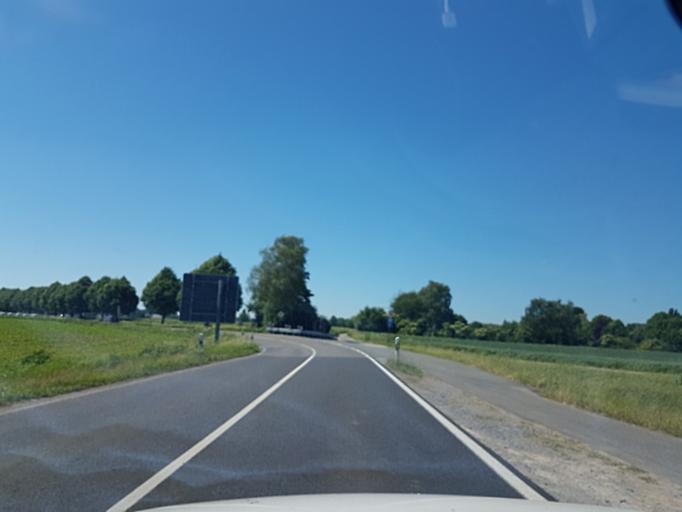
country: DE
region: North Rhine-Westphalia
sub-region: Regierungsbezirk Dusseldorf
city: Ratingen
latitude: 51.3173
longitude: 6.7623
